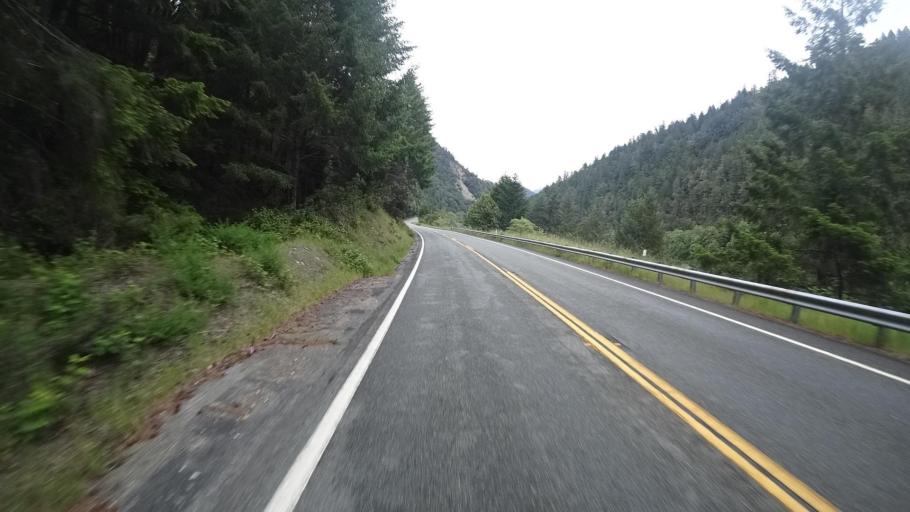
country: US
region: California
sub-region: Humboldt County
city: Willow Creek
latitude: 41.2516
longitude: -123.6379
